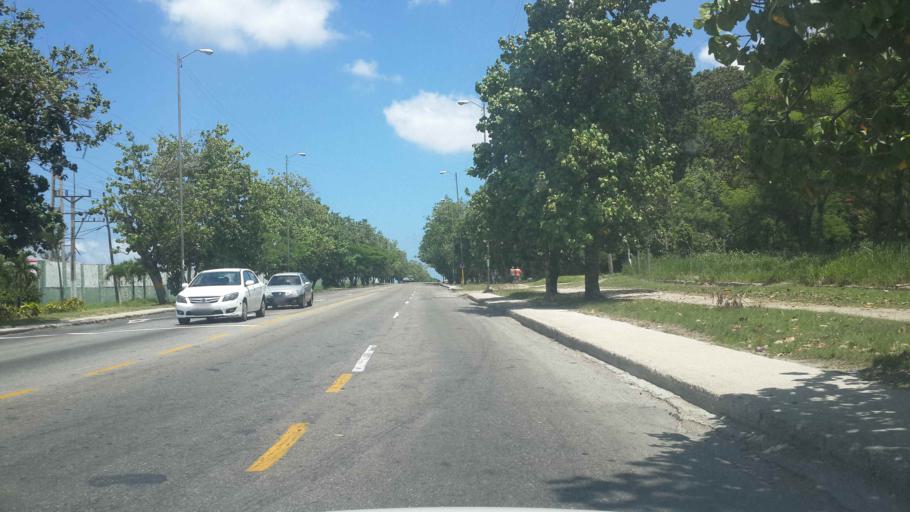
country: CU
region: La Habana
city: Guanabacoa
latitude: 23.1322
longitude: -82.3123
